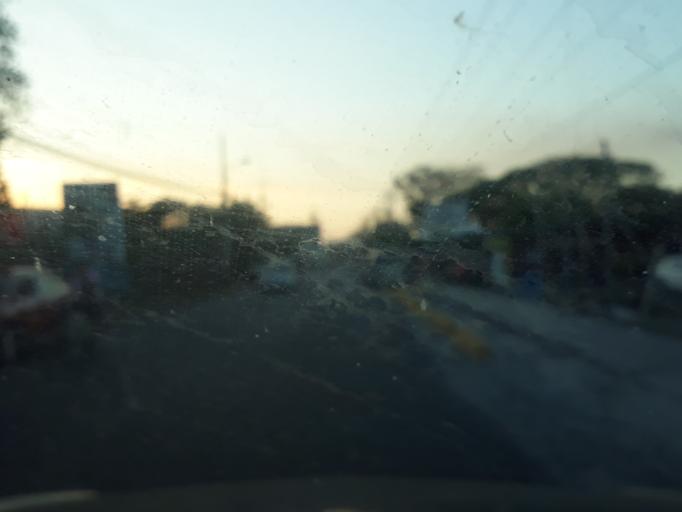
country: CR
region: Puntarenas
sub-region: Canton Central de Puntarenas
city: Chacarita
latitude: 9.9744
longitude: -84.7501
